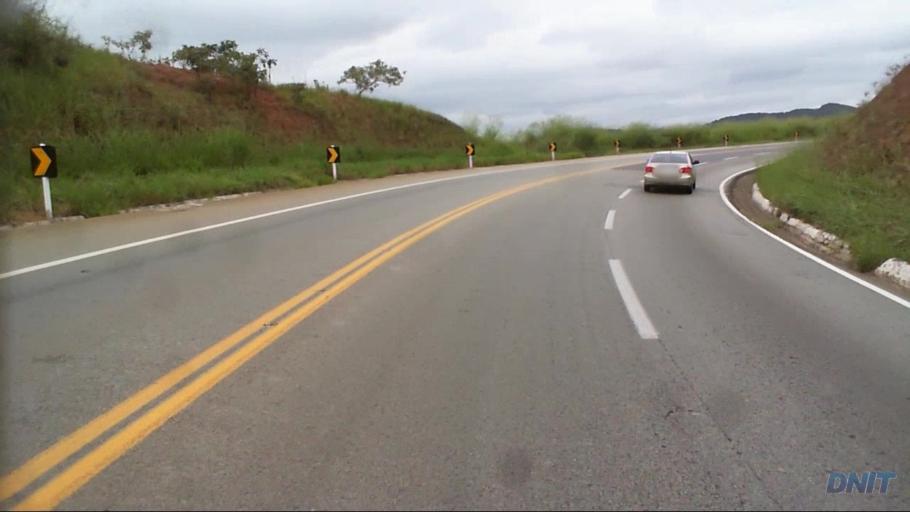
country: BR
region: Minas Gerais
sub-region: Nova Era
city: Nova Era
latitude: -19.7946
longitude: -43.0533
